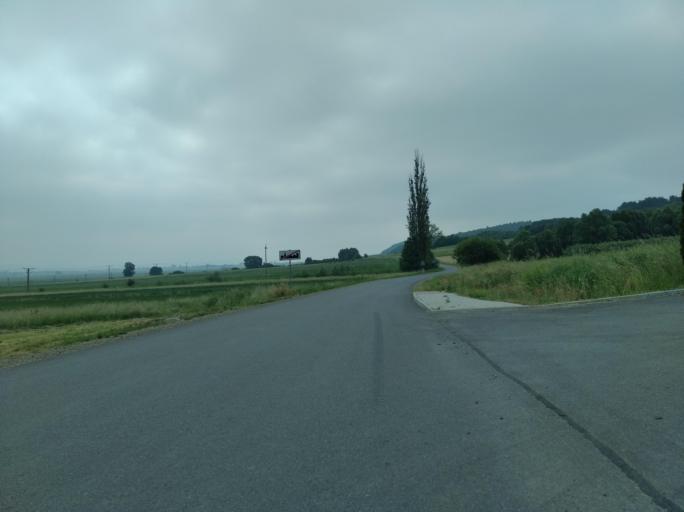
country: PL
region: Subcarpathian Voivodeship
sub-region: Powiat krosnienski
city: Sieniawa
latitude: 49.6010
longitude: 21.9065
